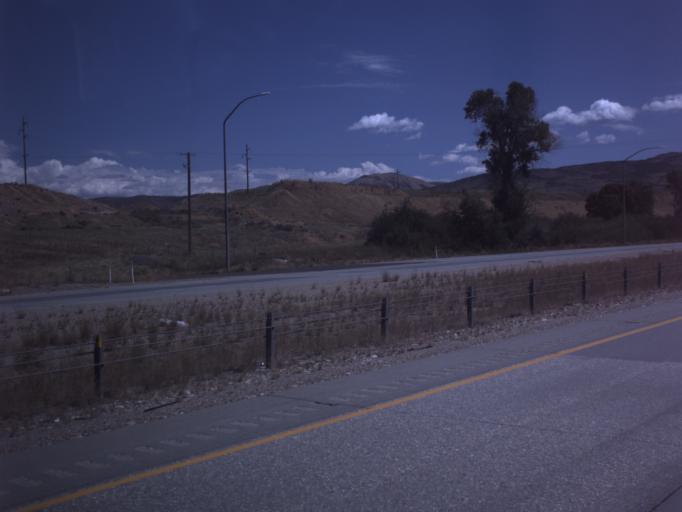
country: US
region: Utah
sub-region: Morgan County
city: Mountain Green
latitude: 41.1372
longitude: -111.7953
